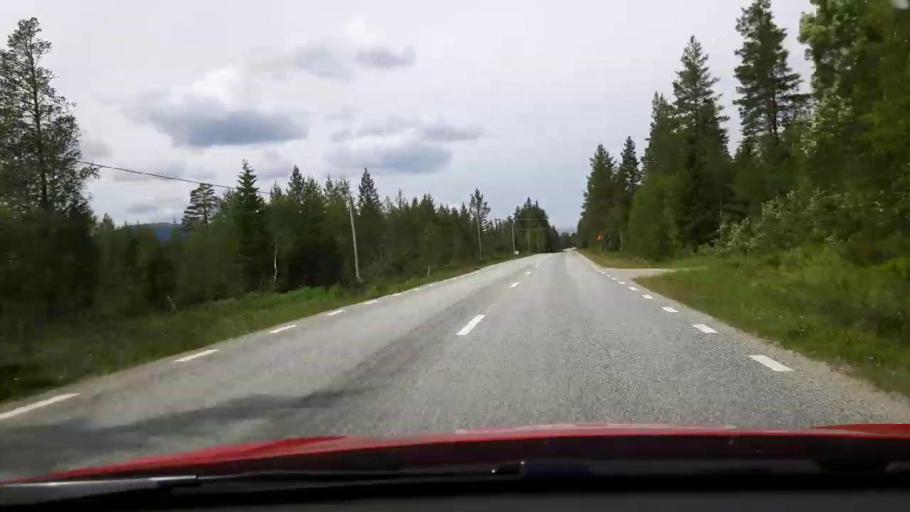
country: SE
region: Jaemtland
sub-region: Harjedalens Kommun
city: Sveg
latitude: 62.1498
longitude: 13.9049
